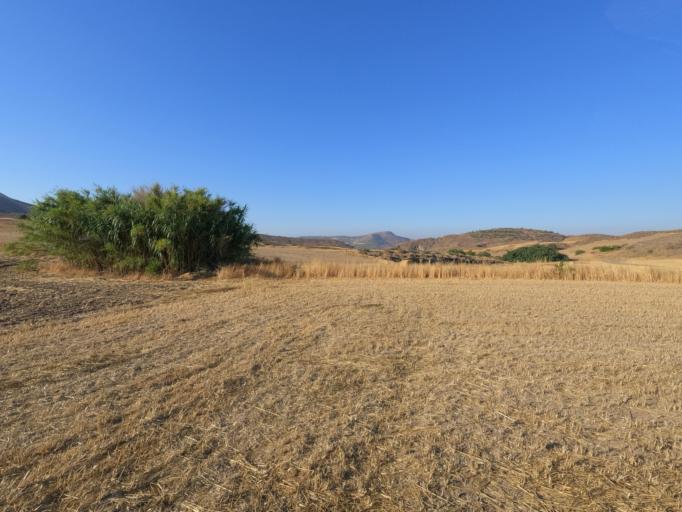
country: CY
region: Larnaka
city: Troulloi
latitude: 35.0234
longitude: 33.6467
